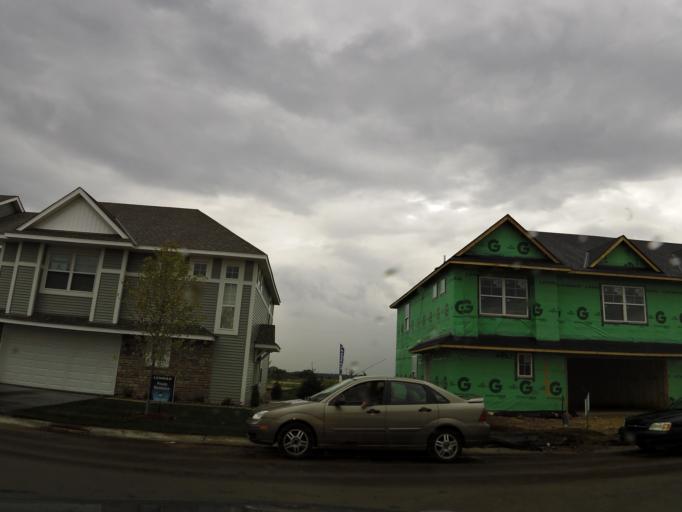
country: US
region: Minnesota
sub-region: Washington County
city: Lake Elmo
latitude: 44.9545
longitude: -92.9045
